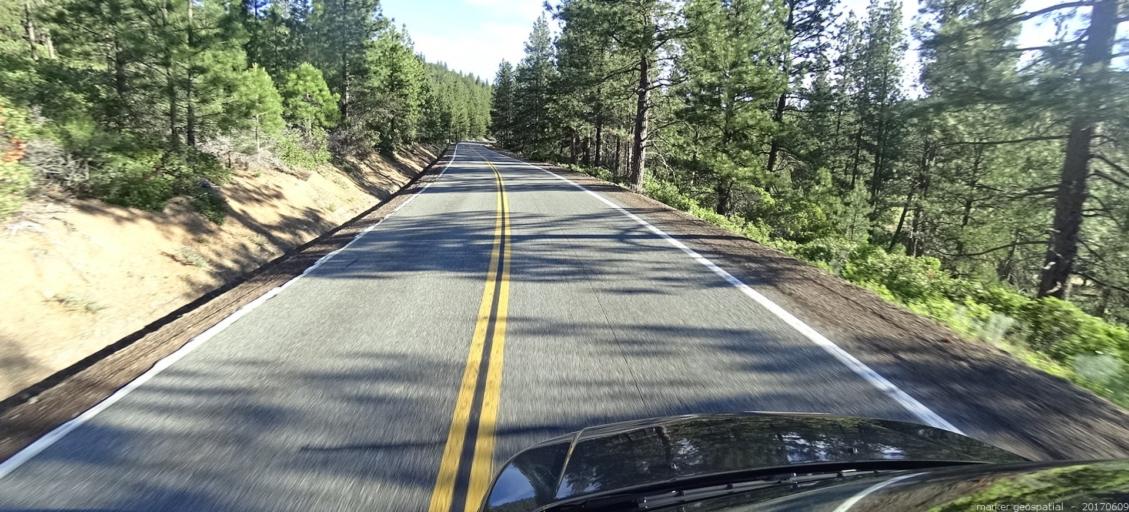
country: US
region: California
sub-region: Siskiyou County
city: Weed
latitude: 41.4285
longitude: -122.6370
